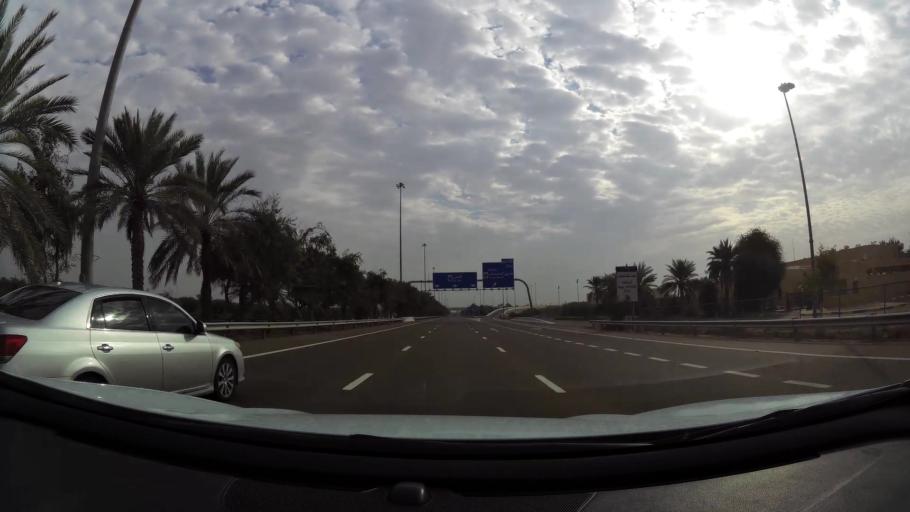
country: AE
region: Abu Dhabi
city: Al Ain
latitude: 24.1810
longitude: 55.3245
